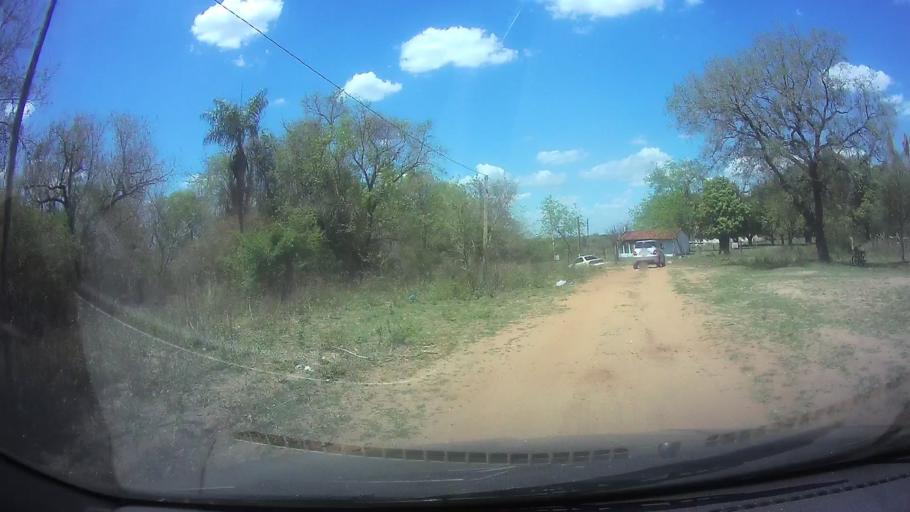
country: PY
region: Cordillera
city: Arroyos y Esteros
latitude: -24.9744
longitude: -57.1939
